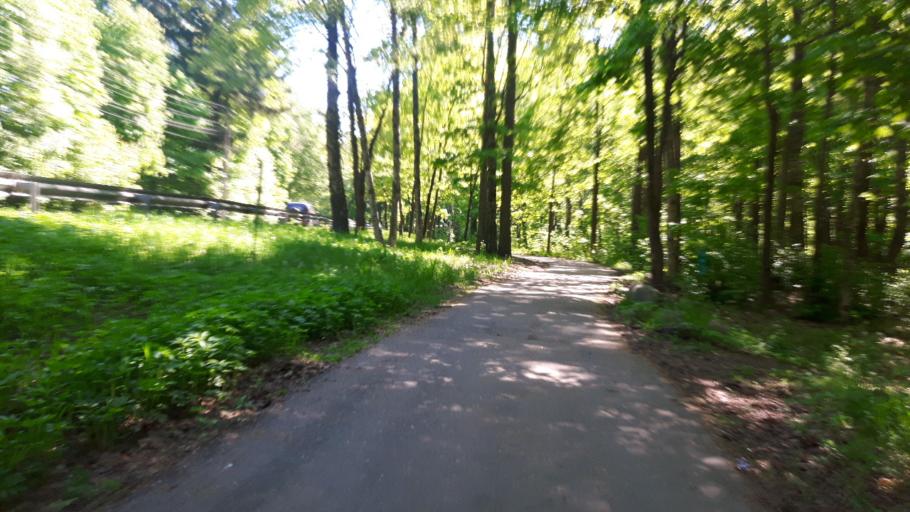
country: RU
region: St.-Petersburg
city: Zelenogorsk
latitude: 60.1929
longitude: 29.6757
